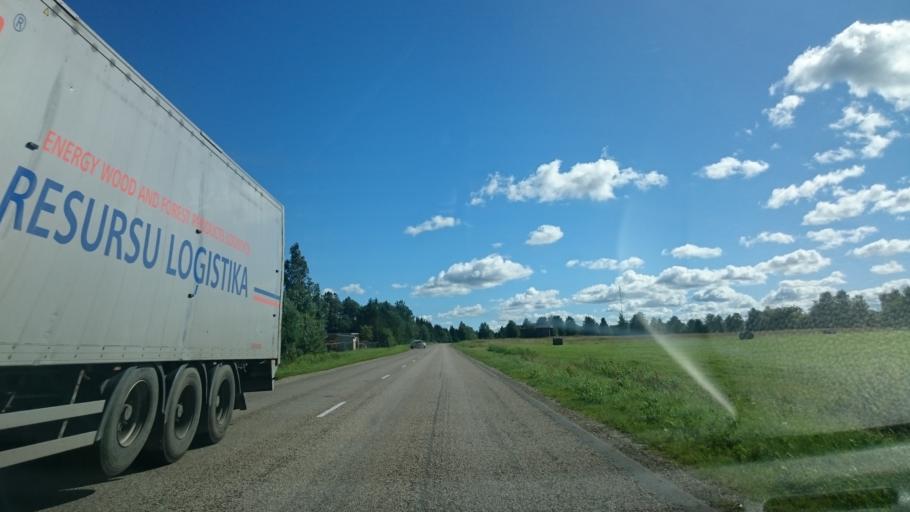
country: LV
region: Aizpute
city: Aizpute
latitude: 56.7442
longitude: 21.6104
